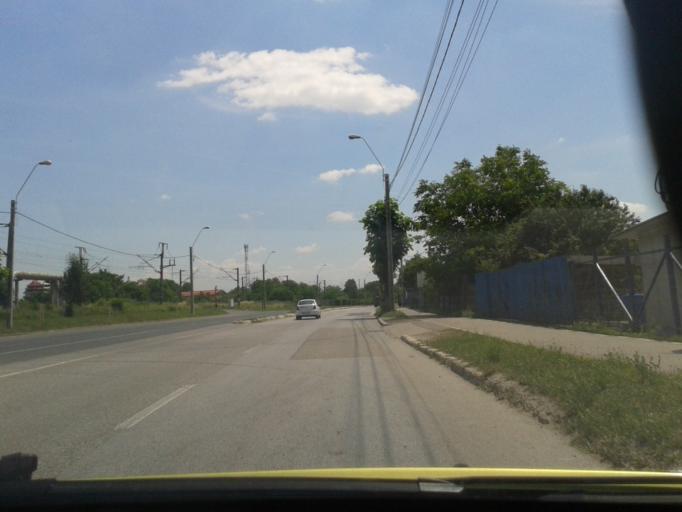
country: RO
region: Hunedoara
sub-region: Municipiul Deva
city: Deva
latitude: 45.8927
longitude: 22.9034
